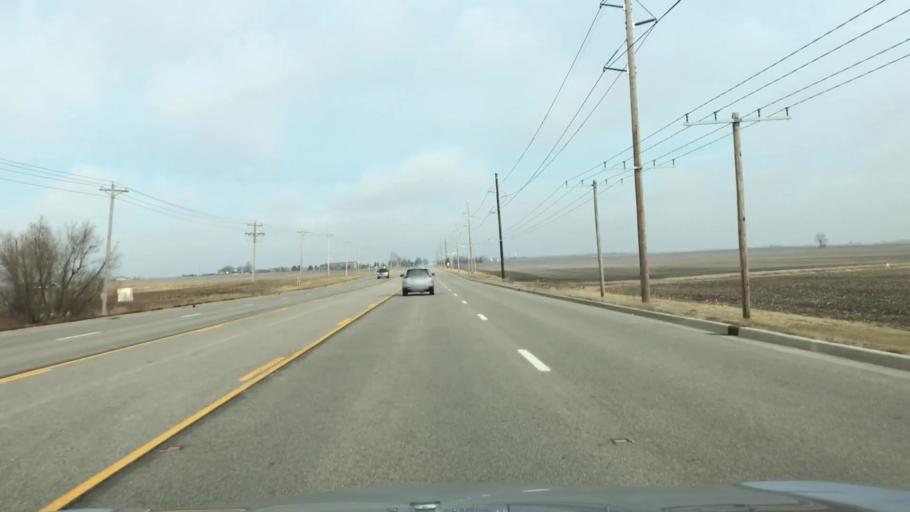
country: US
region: Illinois
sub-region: McLean County
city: Normal
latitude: 40.5215
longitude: -88.9029
